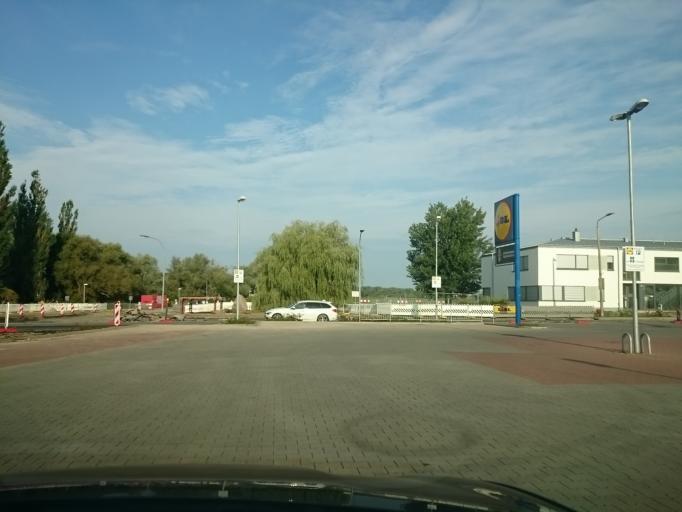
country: DE
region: Mecklenburg-Vorpommern
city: Demmin
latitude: 53.9004
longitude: 13.0433
